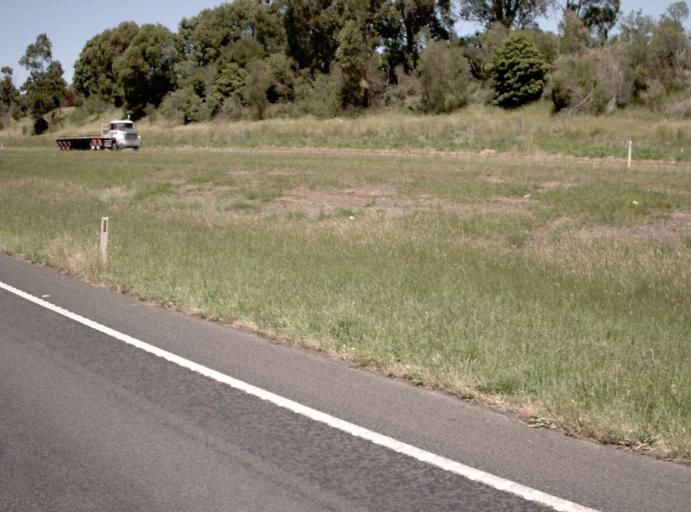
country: AU
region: Victoria
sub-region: Baw Baw
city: Warragul
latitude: -38.1063
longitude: 145.8571
